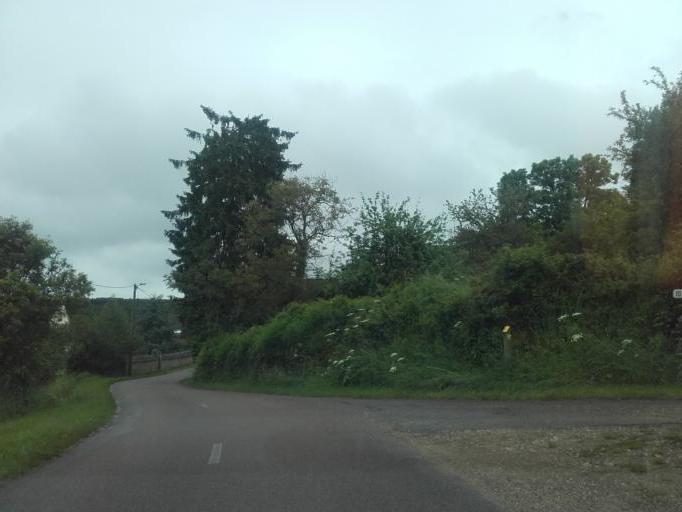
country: FR
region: Bourgogne
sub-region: Departement de la Cote-d'Or
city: Nolay
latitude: 46.9712
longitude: 4.6823
